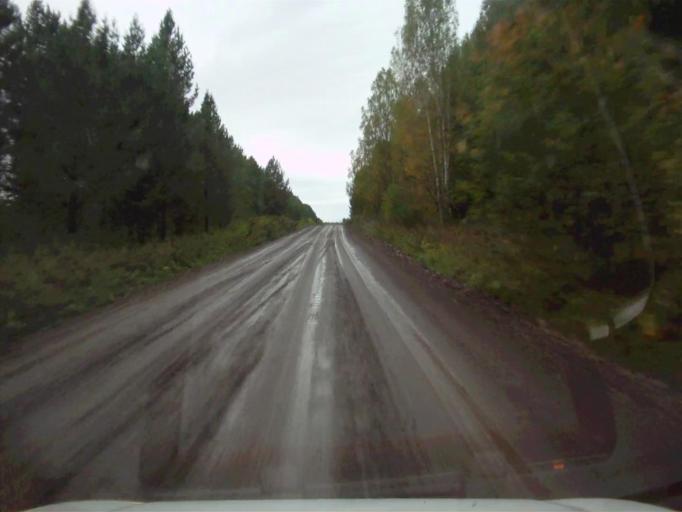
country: RU
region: Chelyabinsk
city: Nyazepetrovsk
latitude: 56.1423
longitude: 59.2897
